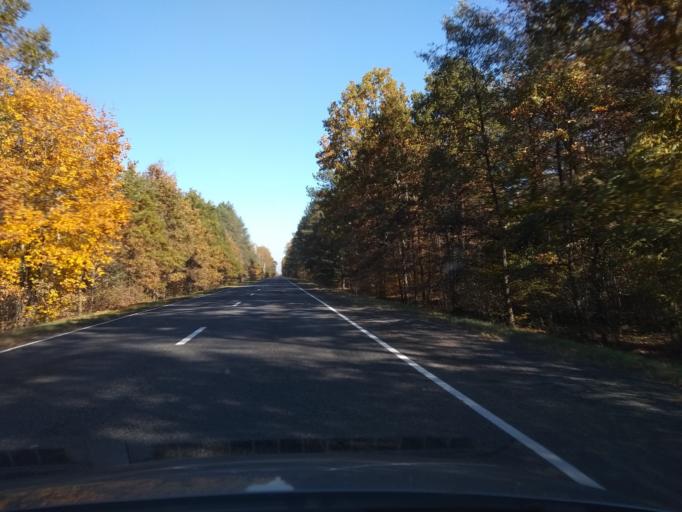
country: BY
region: Brest
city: Malaryta
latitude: 51.9196
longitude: 24.1593
